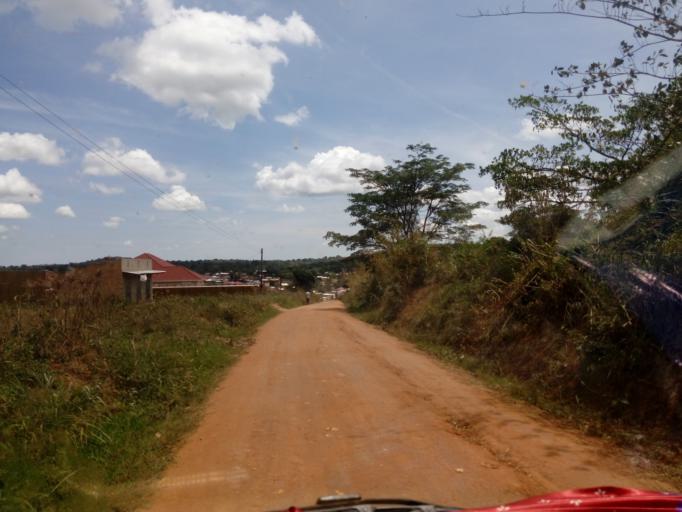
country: UG
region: Central Region
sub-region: Mubende District
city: Mubende
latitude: 0.4504
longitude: 31.6912
